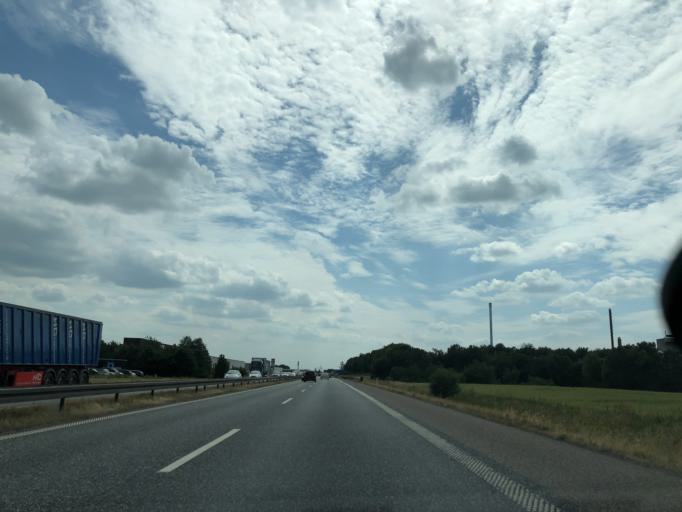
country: DK
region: Central Jutland
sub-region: Hedensted Kommune
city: Hedensted
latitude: 55.8035
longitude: 9.6744
